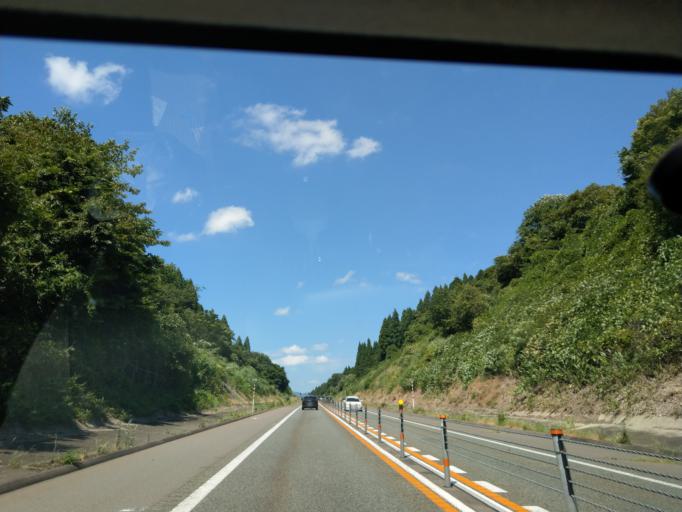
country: JP
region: Akita
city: Akita
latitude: 39.6806
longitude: 140.1856
